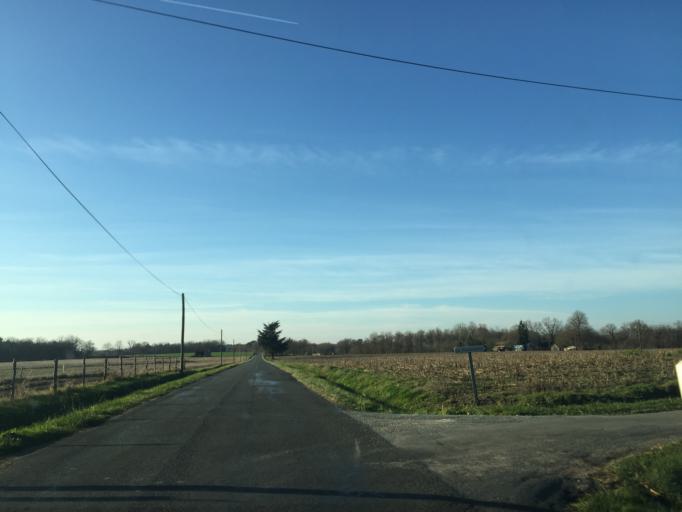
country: FR
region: Aquitaine
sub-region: Departement de la Dordogne
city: Riberac
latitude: 45.2002
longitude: 0.3309
